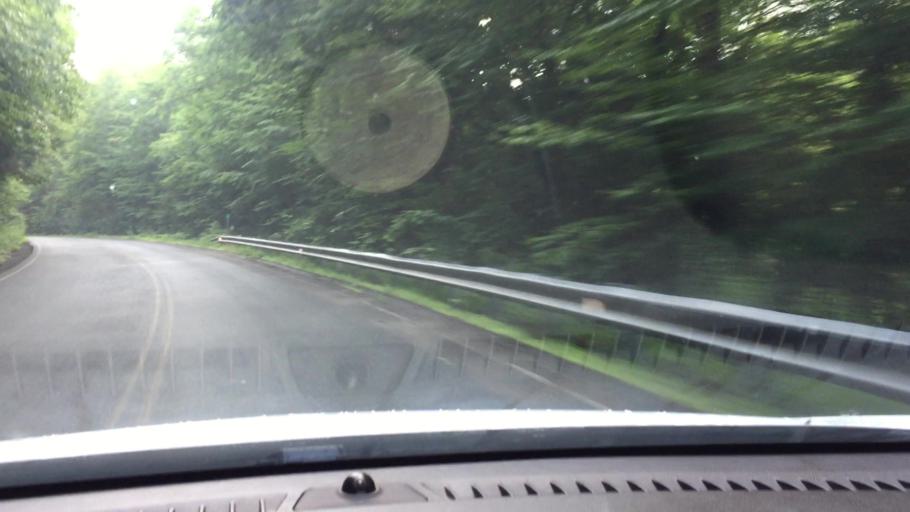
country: US
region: Massachusetts
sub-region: Hampshire County
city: Westhampton
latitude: 42.2483
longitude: -72.9029
